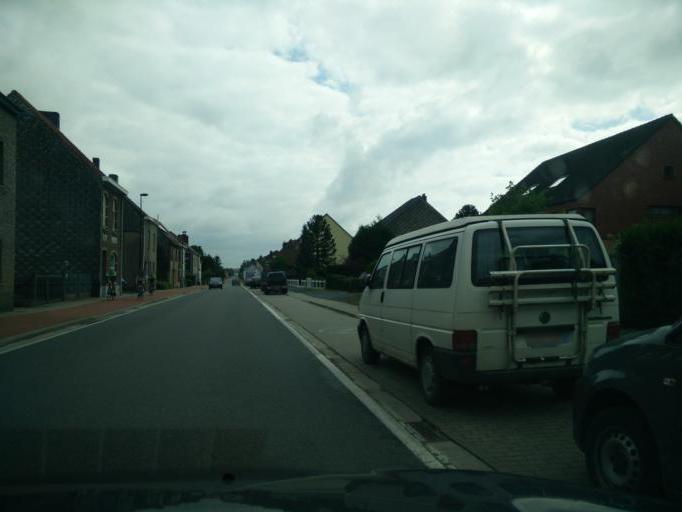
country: BE
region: Flanders
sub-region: Provincie Vlaams-Brabant
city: Beersel
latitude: 50.7321
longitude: 4.3201
